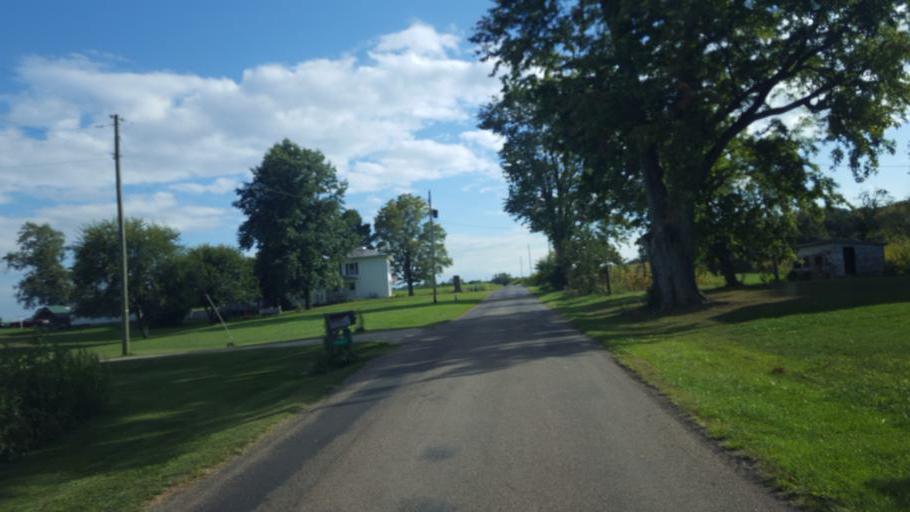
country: US
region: Ohio
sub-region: Knox County
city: Fredericktown
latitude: 40.4341
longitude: -82.5699
